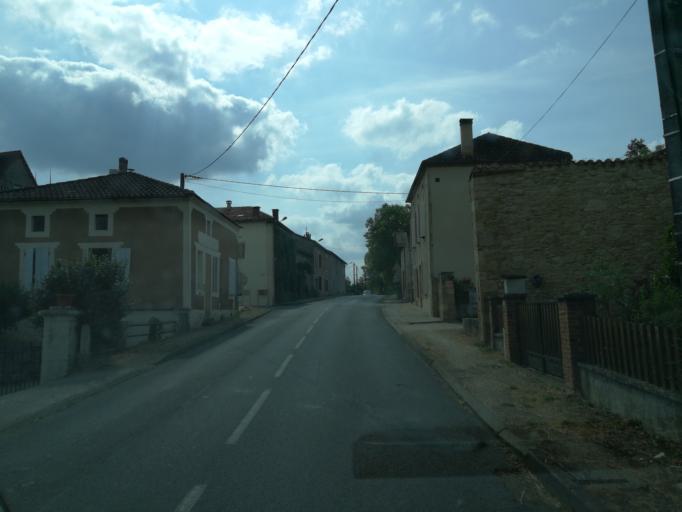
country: FR
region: Aquitaine
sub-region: Departement du Lot-et-Garonne
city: Montayral
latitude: 44.4892
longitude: 1.0175
